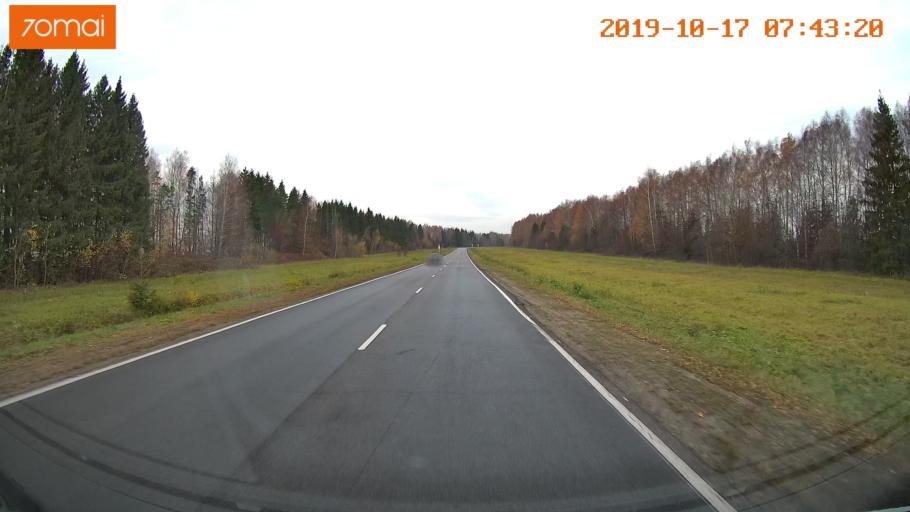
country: RU
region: Vladimir
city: Yur'yev-Pol'skiy
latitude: 56.4823
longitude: 39.7670
